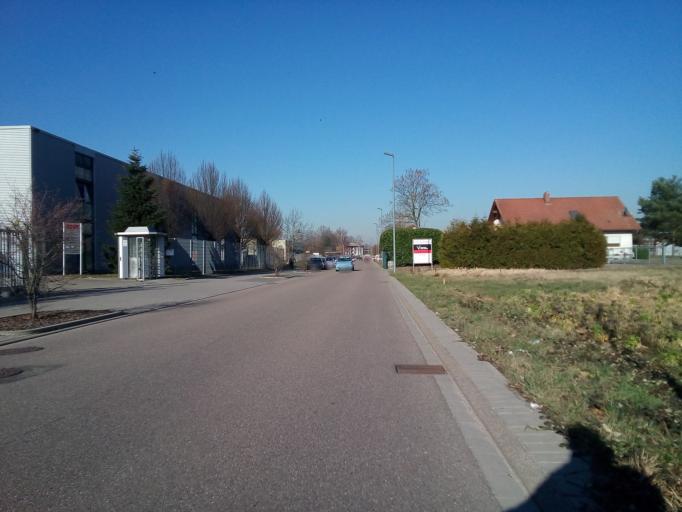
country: DE
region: Baden-Wuerttemberg
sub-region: Karlsruhe Region
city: Buhl
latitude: 48.7052
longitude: 8.1318
